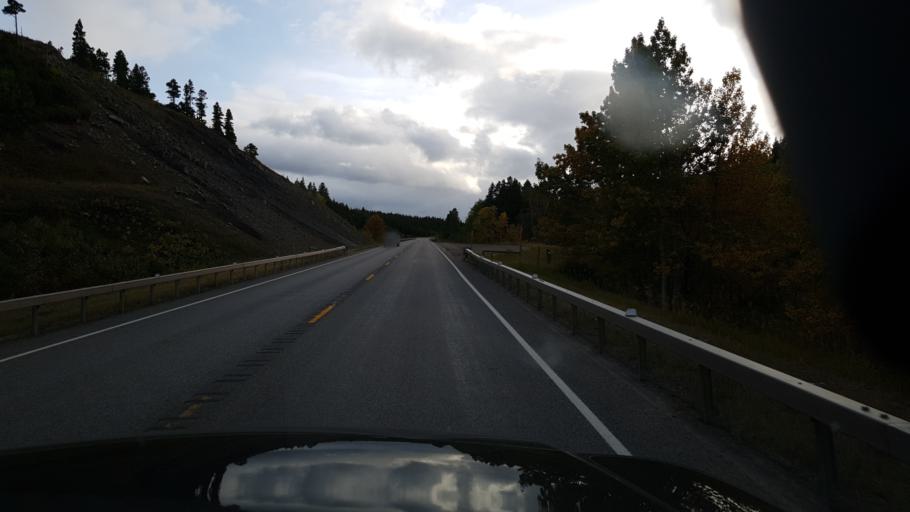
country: US
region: Montana
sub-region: Glacier County
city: South Browning
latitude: 48.3966
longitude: -113.2547
